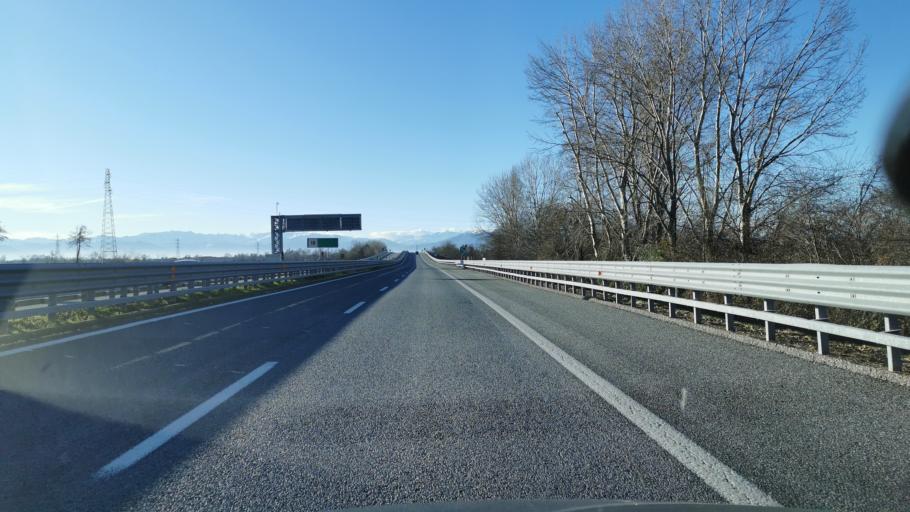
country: IT
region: Piedmont
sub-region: Provincia di Cuneo
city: Trinita
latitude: 44.4692
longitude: 7.7560
